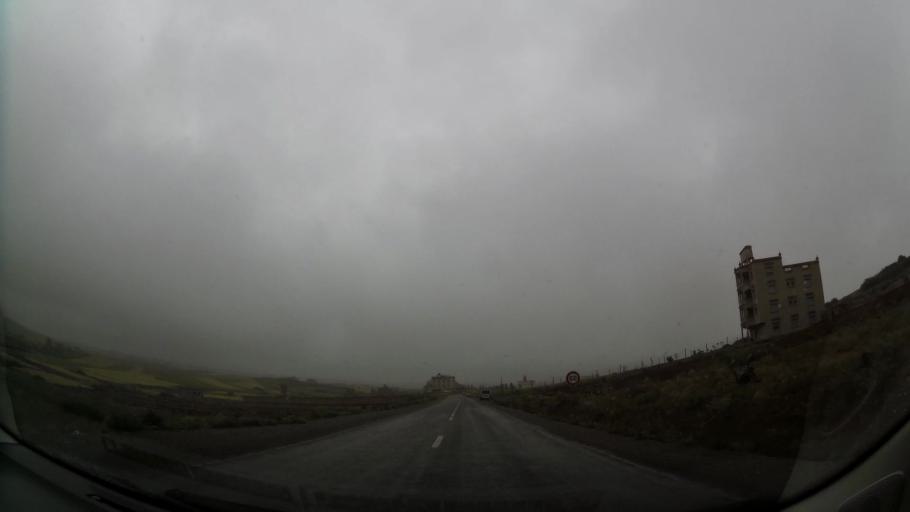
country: MA
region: Oriental
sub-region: Nador
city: Boudinar
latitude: 35.1398
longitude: -3.6103
